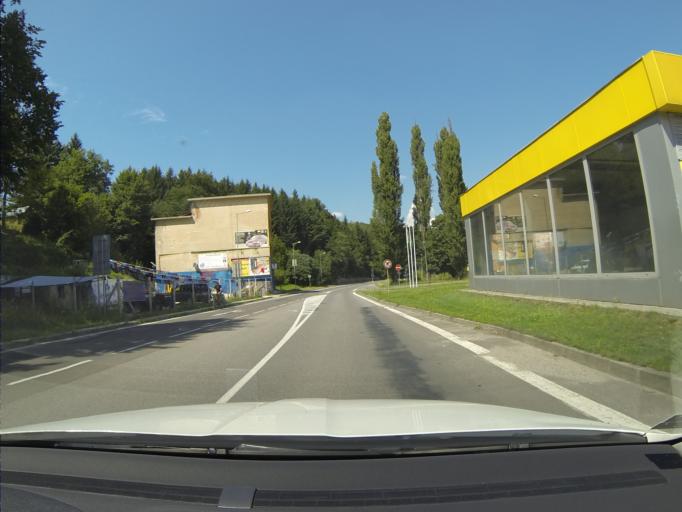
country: SK
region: Nitriansky
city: Handlova
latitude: 48.7379
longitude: 18.7613
